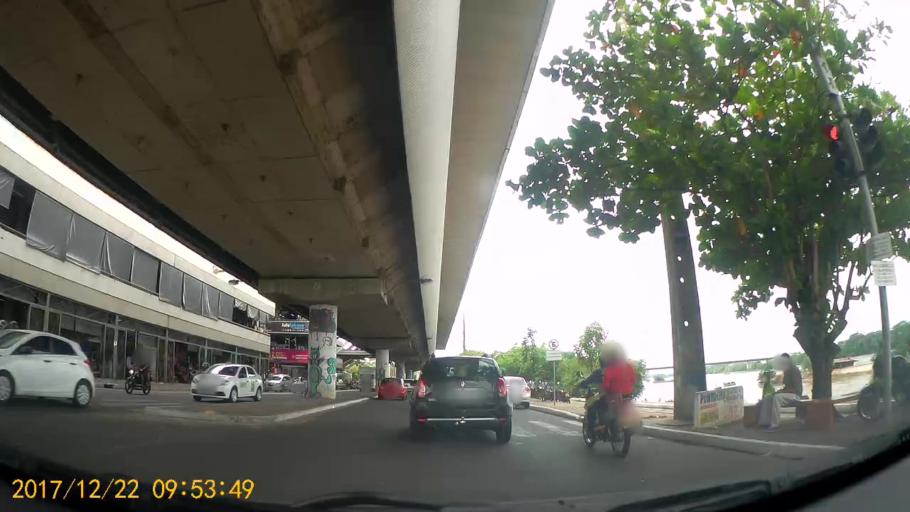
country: BR
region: Piaui
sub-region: Teresina
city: Teresina
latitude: -5.0921
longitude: -42.8189
